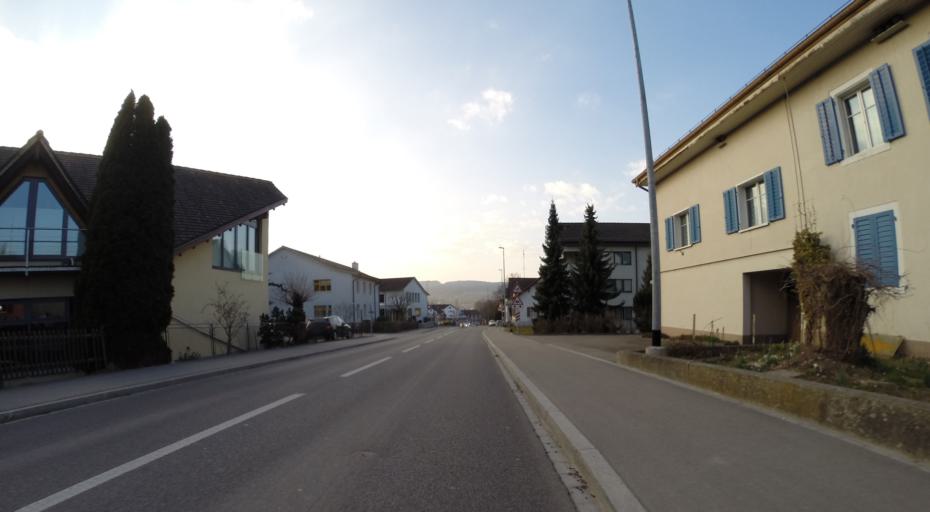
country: CH
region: Thurgau
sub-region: Frauenfeld District
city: Steckborn
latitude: 47.6644
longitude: 8.9845
